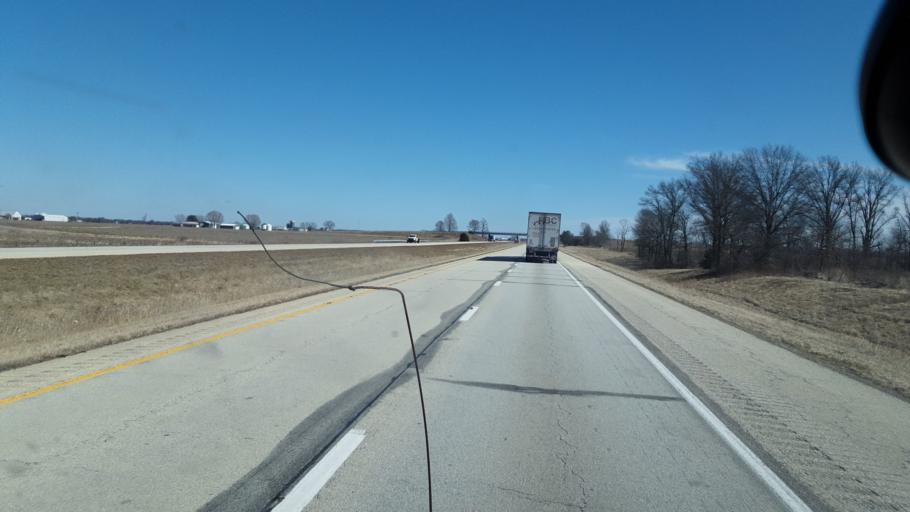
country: US
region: Illinois
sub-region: Effingham County
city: Teutopolis
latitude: 39.1578
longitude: -88.4504
